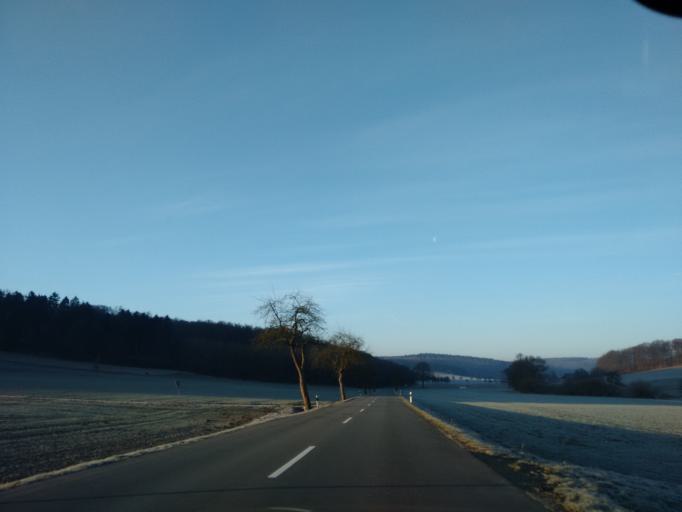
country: DE
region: North Rhine-Westphalia
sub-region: Regierungsbezirk Detmold
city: Altenbeken
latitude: 51.7022
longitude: 8.8973
